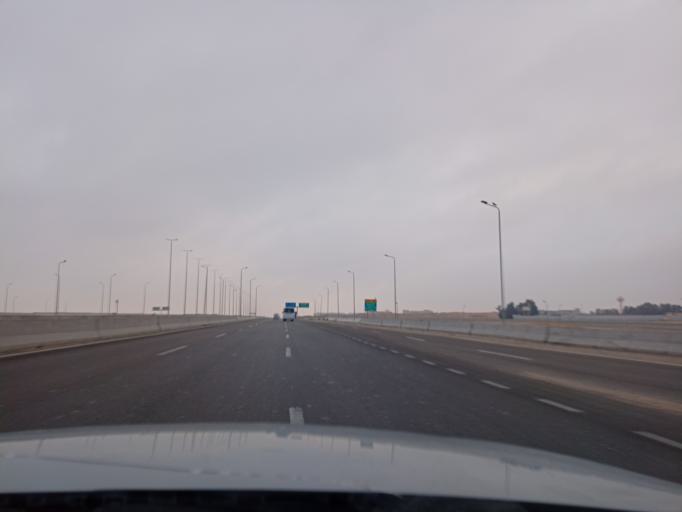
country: EG
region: Muhafazat al Qalyubiyah
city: Al Khankah
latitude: 30.0838
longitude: 31.4536
